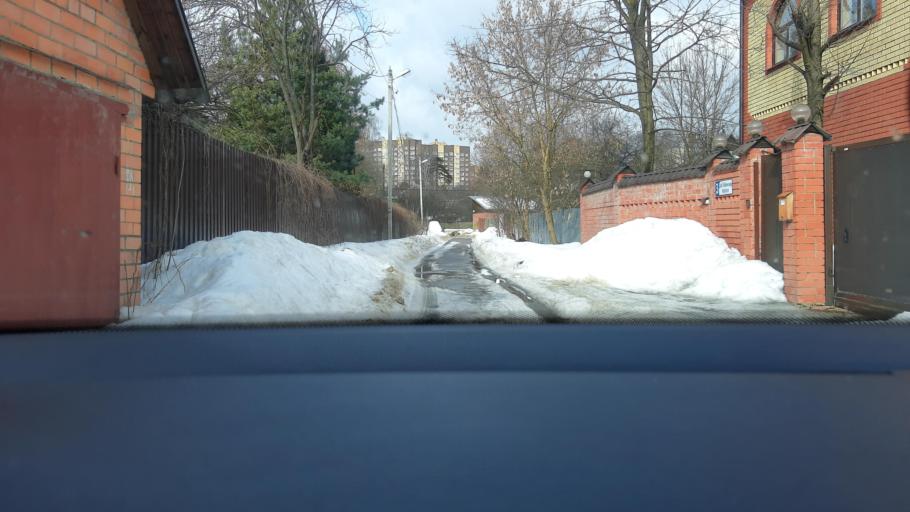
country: RU
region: Moskovskaya
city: Druzhba
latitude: 55.8972
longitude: 37.7418
